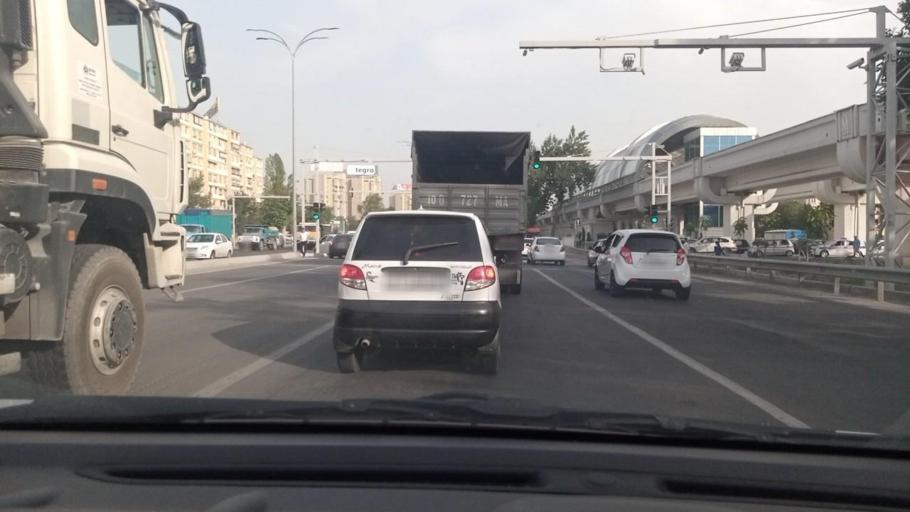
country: UZ
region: Toshkent
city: Salor
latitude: 41.2933
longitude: 69.3555
